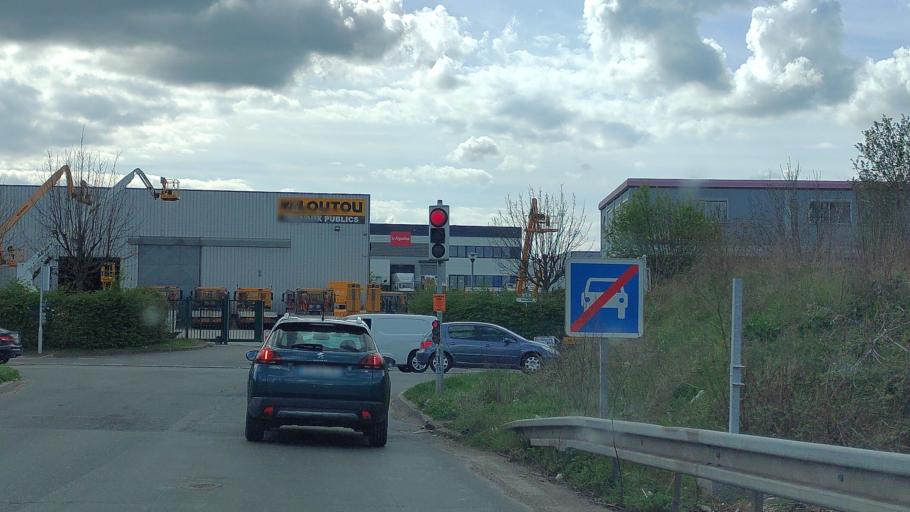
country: FR
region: Ile-de-France
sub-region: Departement du Val-d'Oise
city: Saint-Ouen-l'Aumone
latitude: 49.0518
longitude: 2.1473
